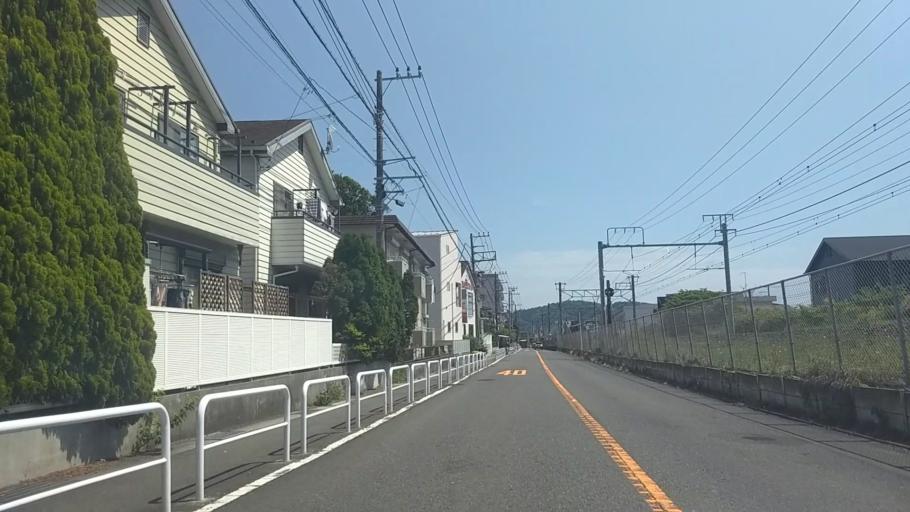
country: JP
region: Kanagawa
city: Zushi
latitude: 35.3035
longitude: 139.5701
